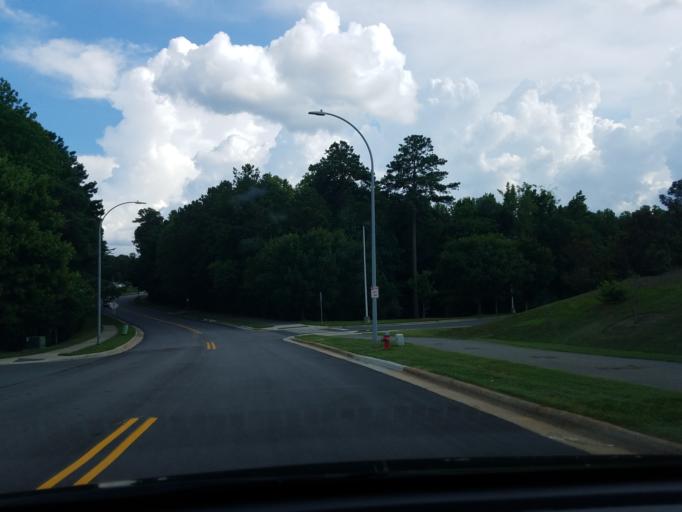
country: US
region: North Carolina
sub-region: Wake County
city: Apex
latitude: 35.7380
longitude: -78.8099
